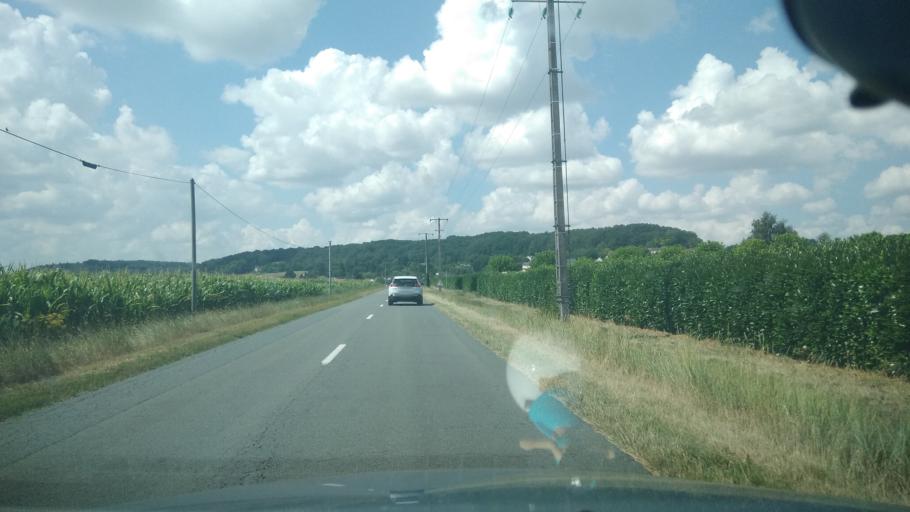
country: FR
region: Poitou-Charentes
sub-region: Departement de la Vienne
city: Dange-Saint-Romain
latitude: 46.9131
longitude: 0.5746
